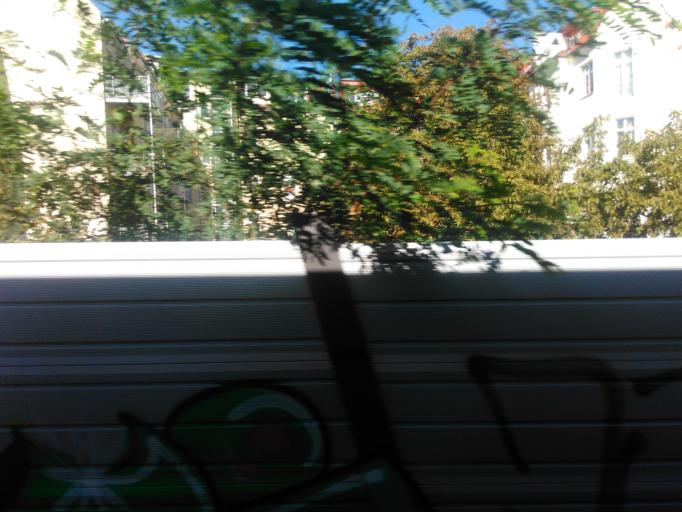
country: DE
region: Berlin
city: Friedrichshain Bezirk
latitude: 52.5052
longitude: 13.4704
